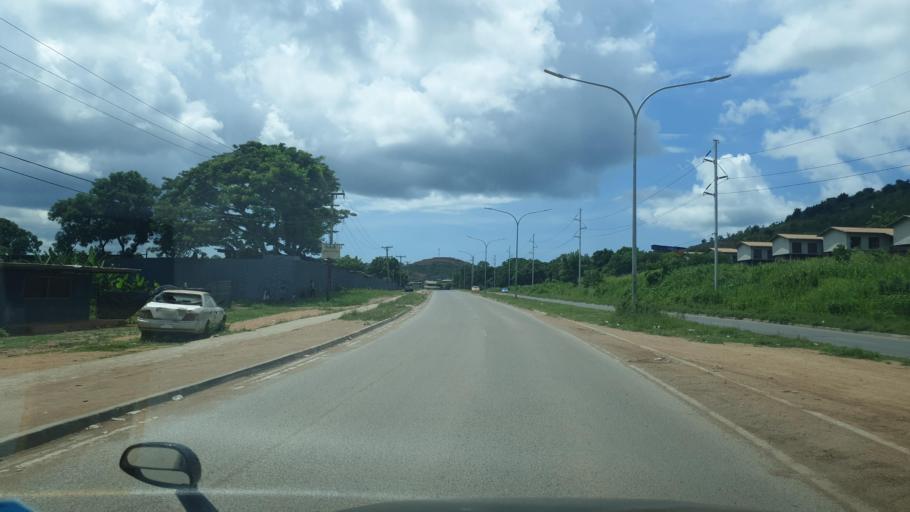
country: PG
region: National Capital
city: Port Moresby
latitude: -9.3899
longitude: 147.1533
